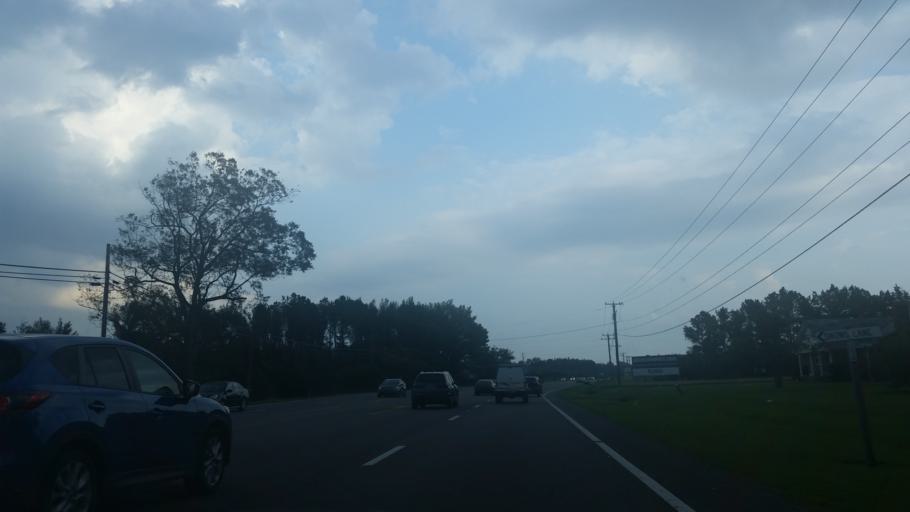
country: US
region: North Carolina
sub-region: Dare County
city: Southern Shores
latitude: 36.1404
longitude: -75.8422
